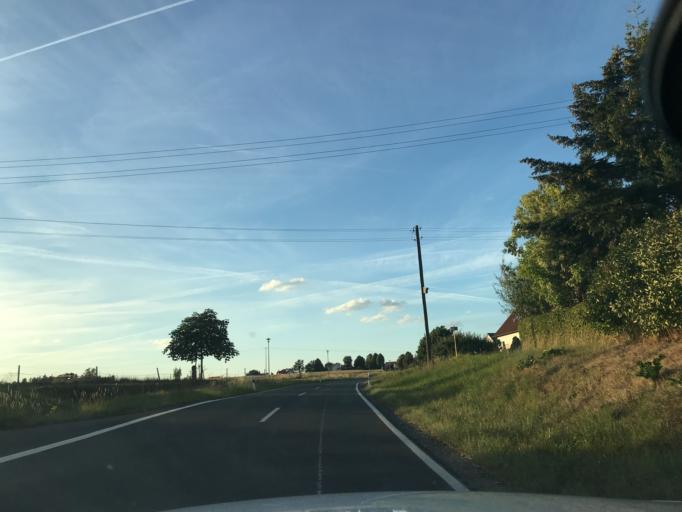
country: DE
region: Bavaria
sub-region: Upper Franconia
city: Pegnitz
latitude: 49.7099
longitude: 11.5759
